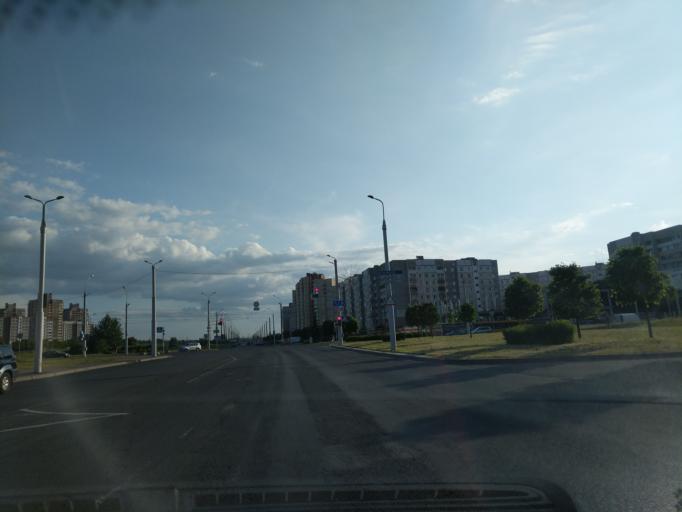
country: BY
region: Minsk
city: Malinovka
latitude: 53.8550
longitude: 27.4477
